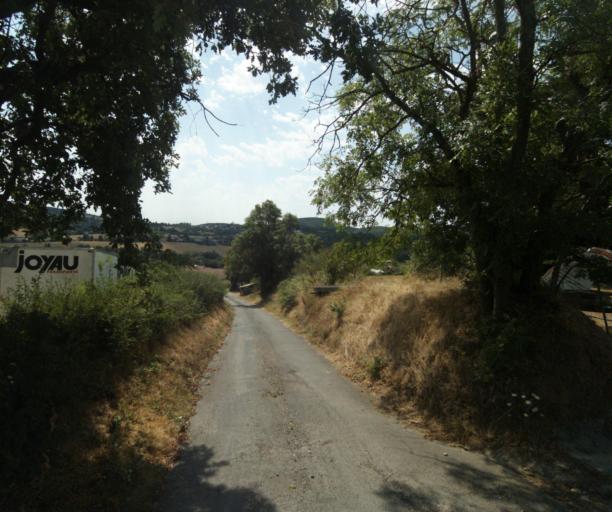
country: FR
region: Rhone-Alpes
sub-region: Departement du Rhone
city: Lentilly
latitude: 45.8171
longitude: 4.6433
